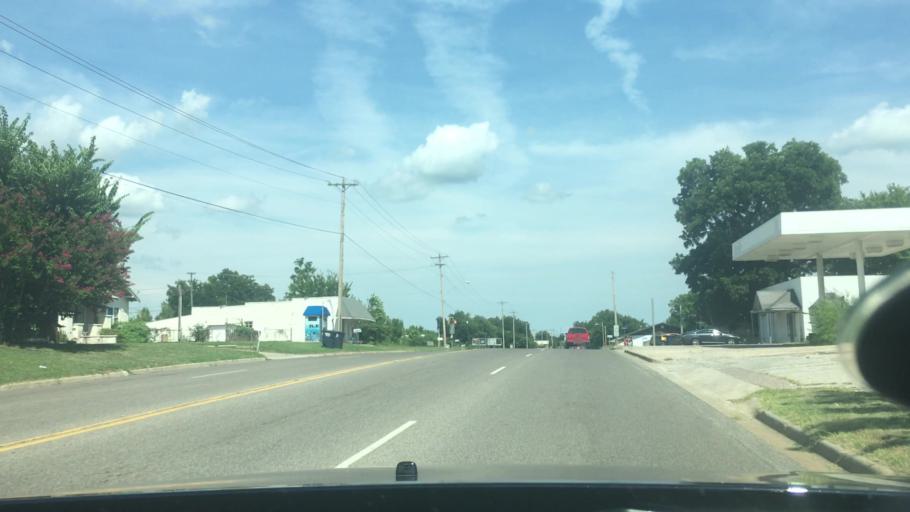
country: US
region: Oklahoma
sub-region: Pottawatomie County
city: Shawnee
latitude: 35.3327
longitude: -96.9047
